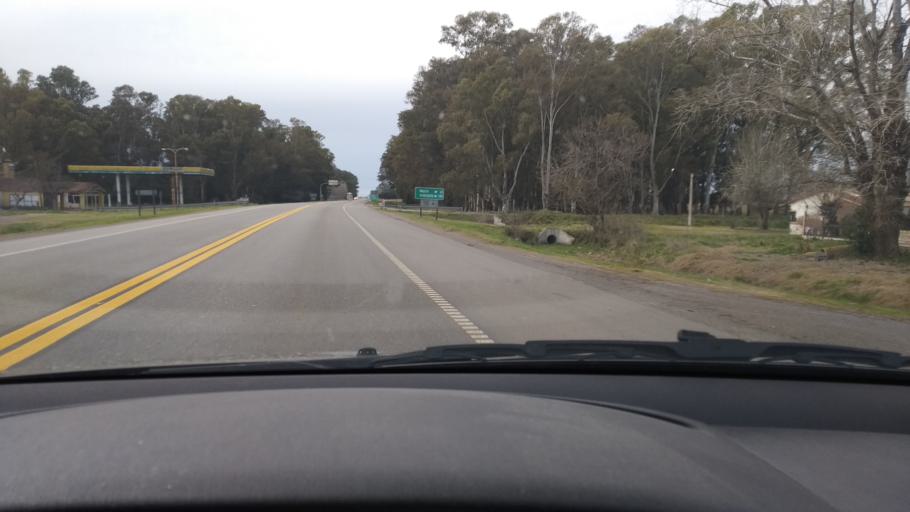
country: AR
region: Buenos Aires
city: Tapalque
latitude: -36.3859
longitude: -59.4905
